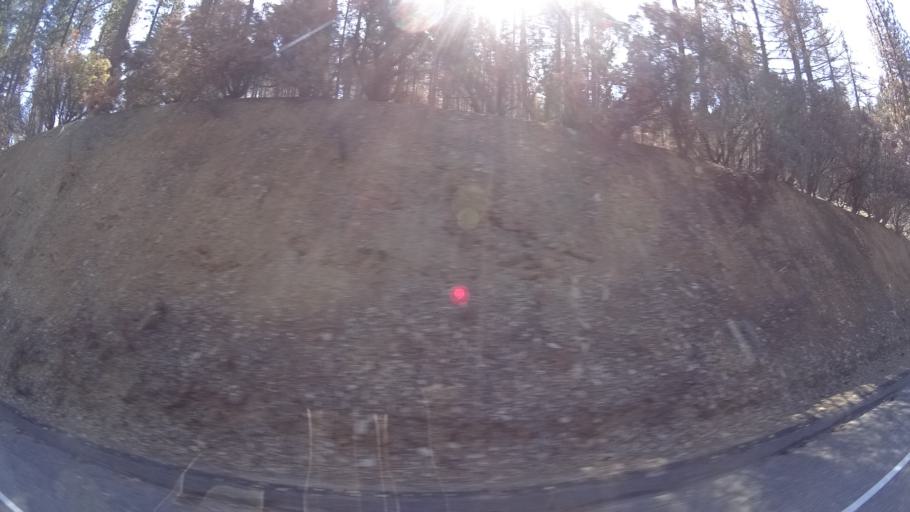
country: US
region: California
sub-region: Tehama County
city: Rancho Tehama Reserve
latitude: 39.6614
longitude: -122.7214
